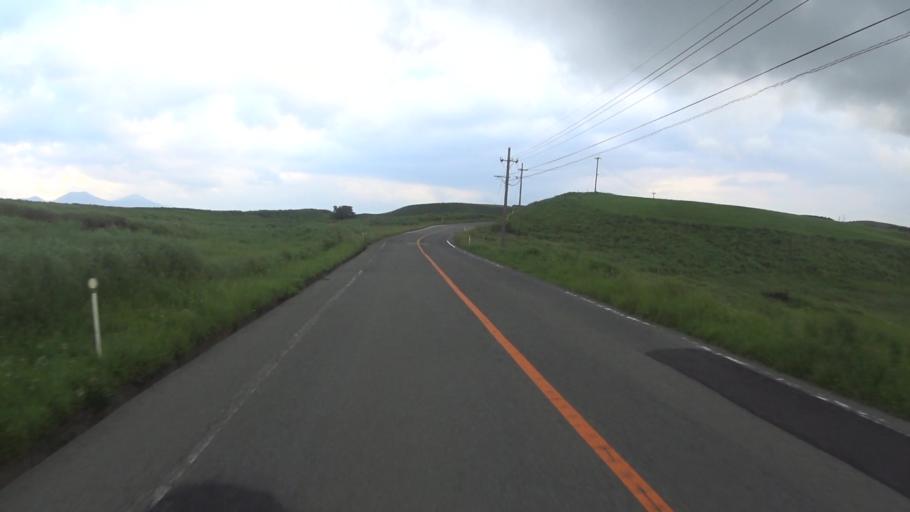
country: JP
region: Kumamoto
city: Aso
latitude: 32.9663
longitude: 131.0016
